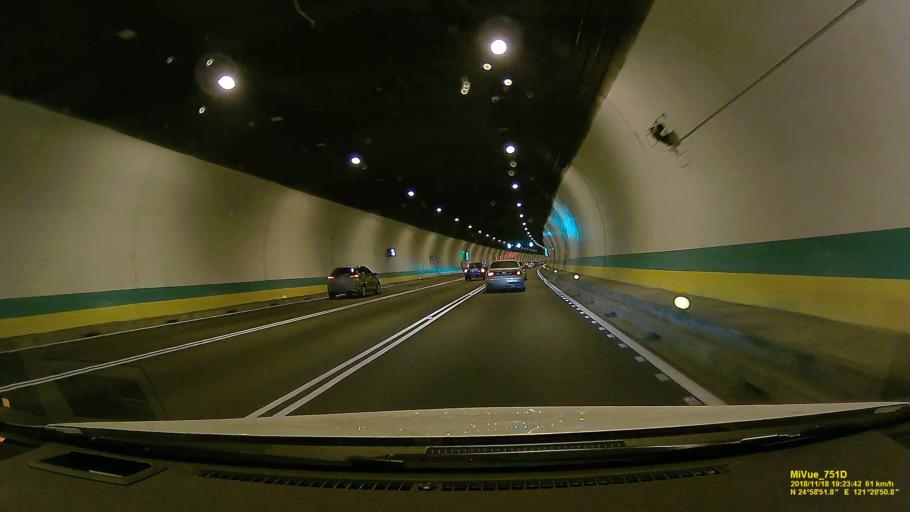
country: TW
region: Taipei
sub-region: Taipei
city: Banqiao
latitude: 24.9815
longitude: 121.4963
